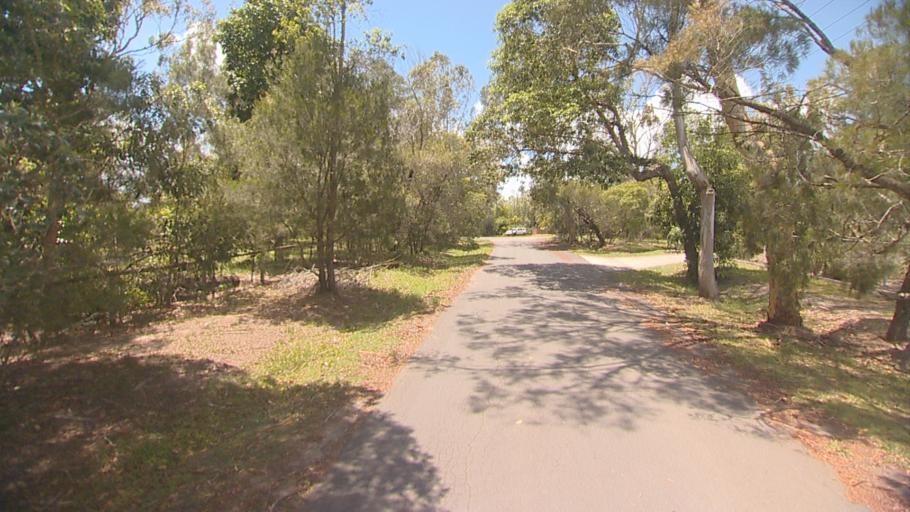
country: AU
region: Queensland
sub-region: Redland
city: Redland Bay
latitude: -27.6704
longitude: 153.2773
